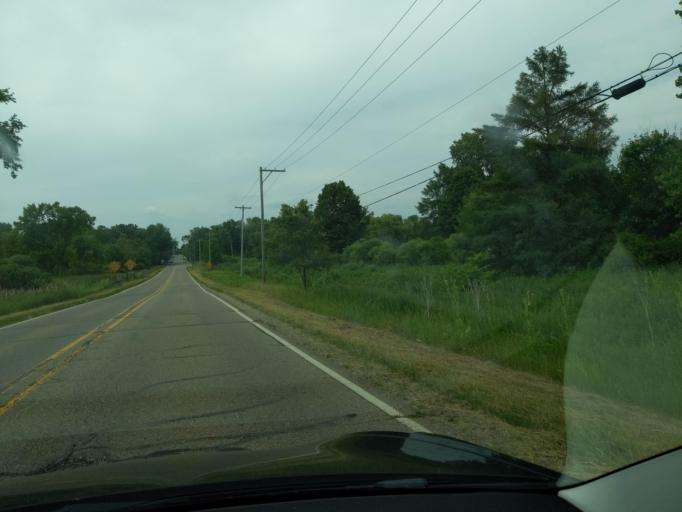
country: US
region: Michigan
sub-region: Clinton County
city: DeWitt
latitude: 42.8204
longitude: -84.6027
